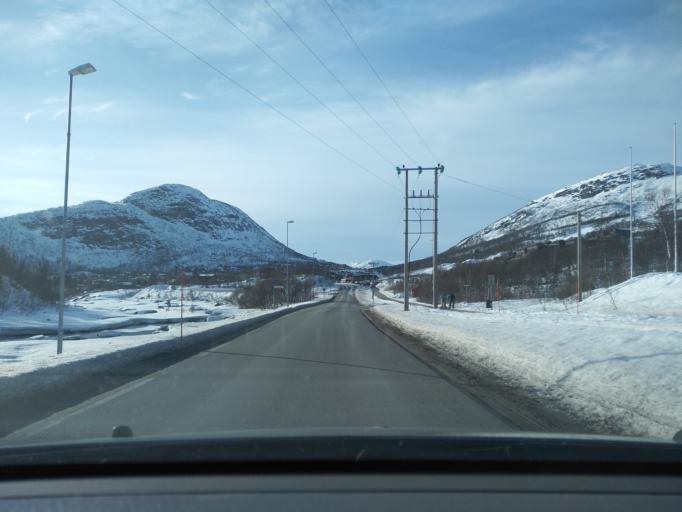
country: NO
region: Aust-Agder
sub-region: Bykle
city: Hovden
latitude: 59.5688
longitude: 7.3572
